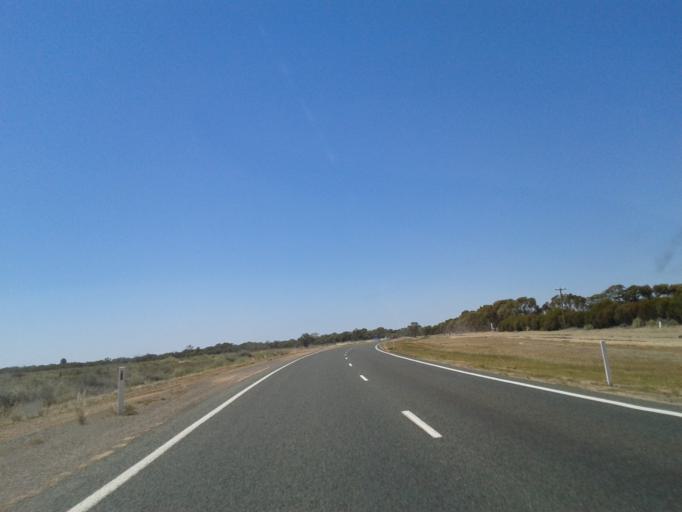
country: AU
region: New South Wales
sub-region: Wentworth
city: Dareton
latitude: -34.1108
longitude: 141.9493
